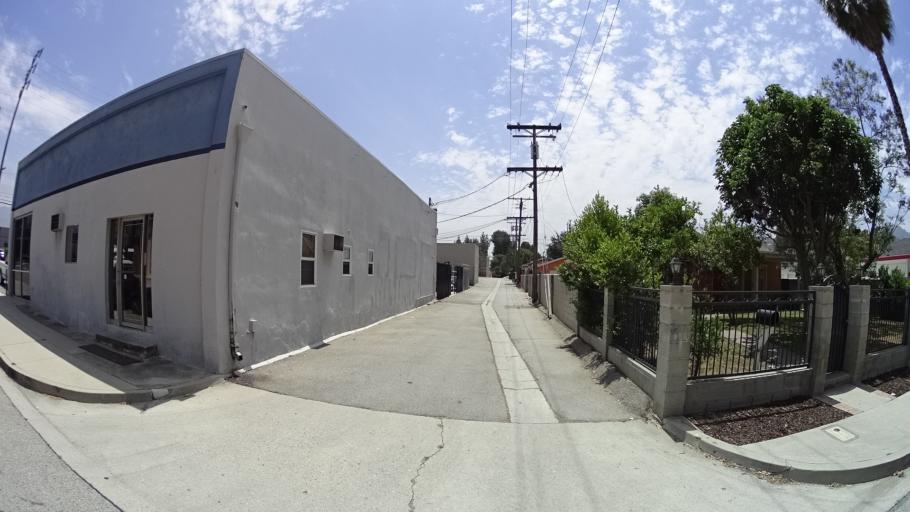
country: US
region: California
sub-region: Los Angeles County
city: Burbank
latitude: 34.1629
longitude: -118.3036
